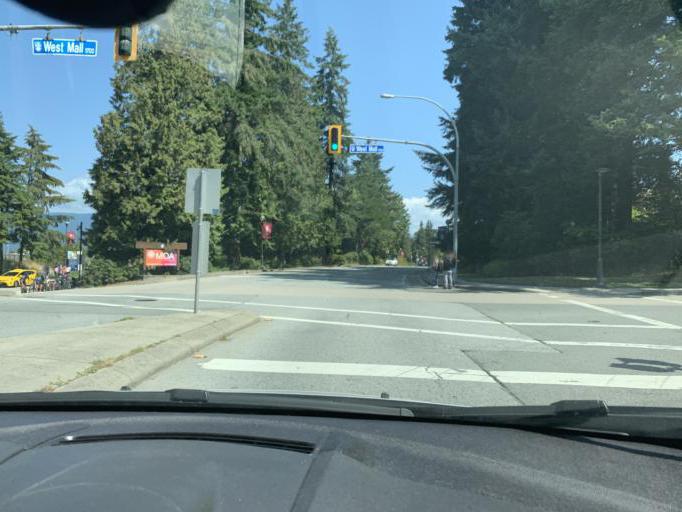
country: CA
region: British Columbia
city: West End
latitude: 49.2685
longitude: -123.2589
